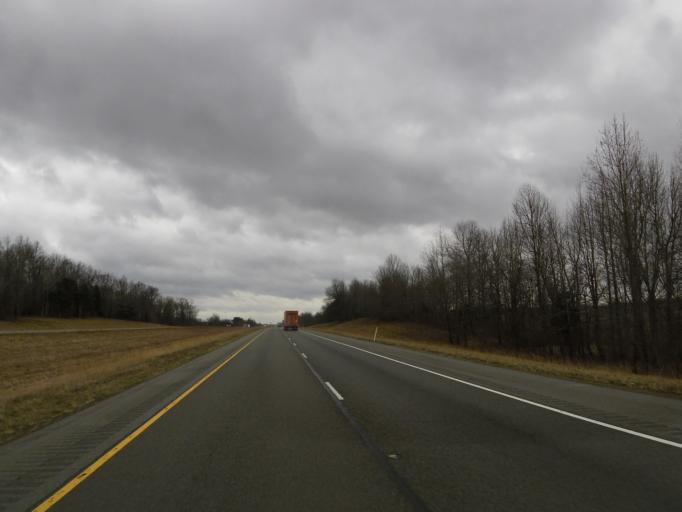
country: US
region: Illinois
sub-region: Massac County
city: Metropolis
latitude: 37.2086
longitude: -88.6960
